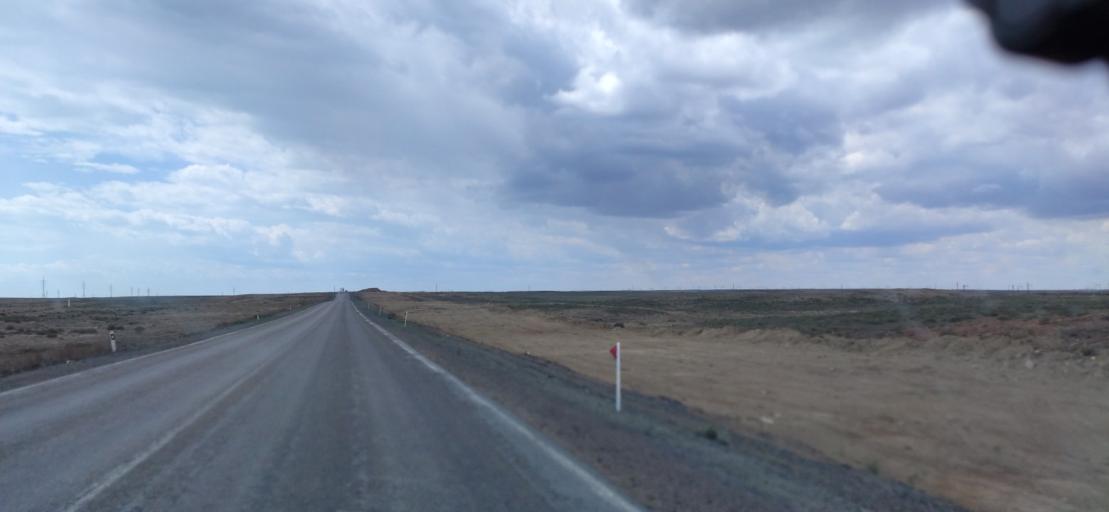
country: KZ
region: Qaraghandy
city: Saryshaghan
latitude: 46.0809
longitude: 73.6045
